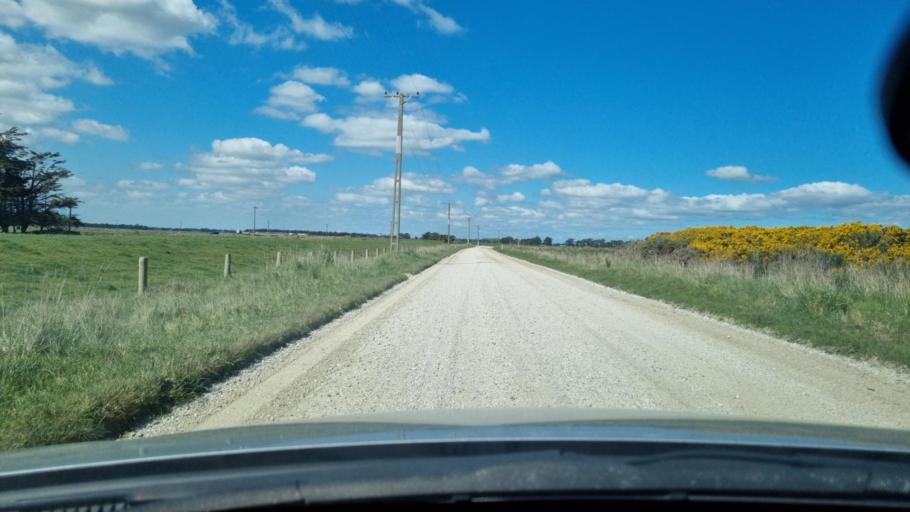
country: NZ
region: Southland
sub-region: Invercargill City
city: Invercargill
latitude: -46.3919
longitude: 168.2696
